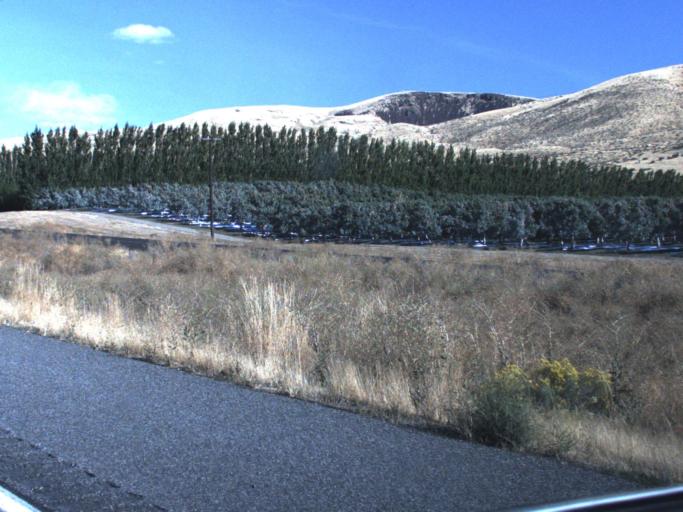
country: US
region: Washington
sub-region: Benton County
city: Benton City
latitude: 46.2550
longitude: -119.5985
